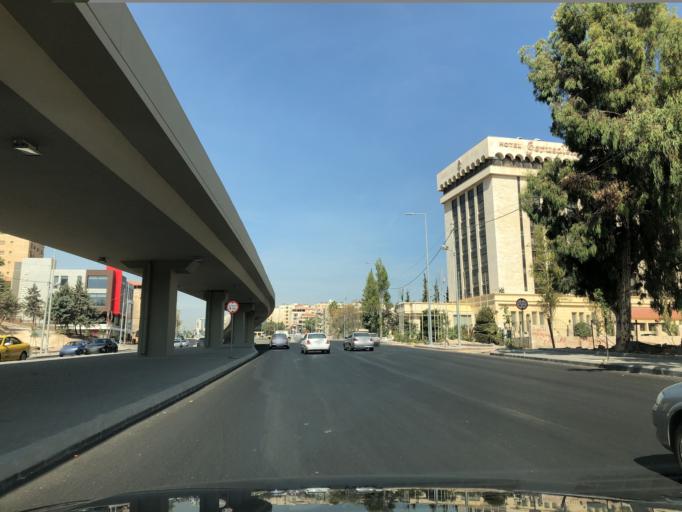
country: JO
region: Amman
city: Al Jubayhah
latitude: 31.9906
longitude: 35.8927
